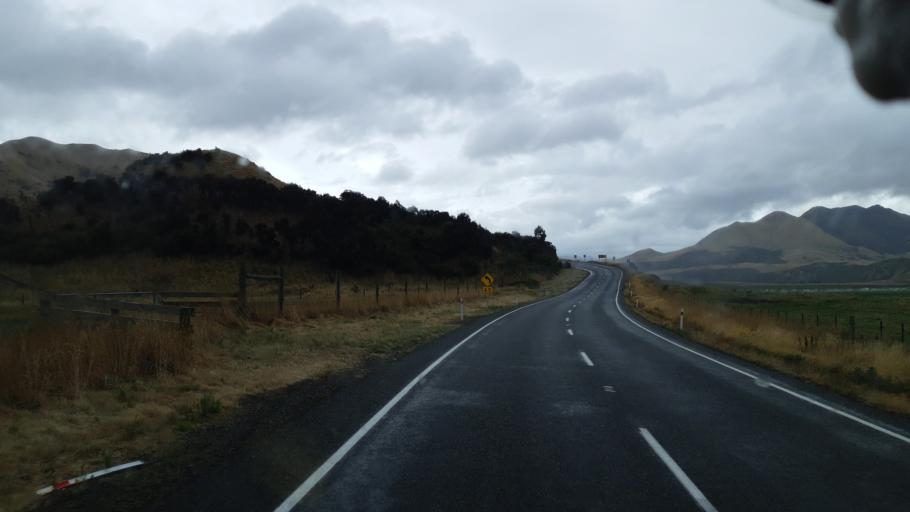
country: NZ
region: Canterbury
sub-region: Hurunui District
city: Amberley
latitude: -42.6442
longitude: 172.7728
